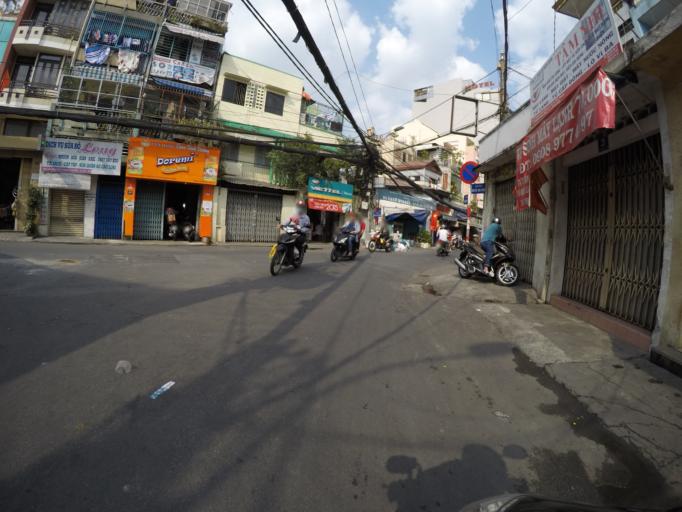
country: VN
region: Ho Chi Minh City
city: Quan Phu Nhuan
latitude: 10.7971
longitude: 106.6801
